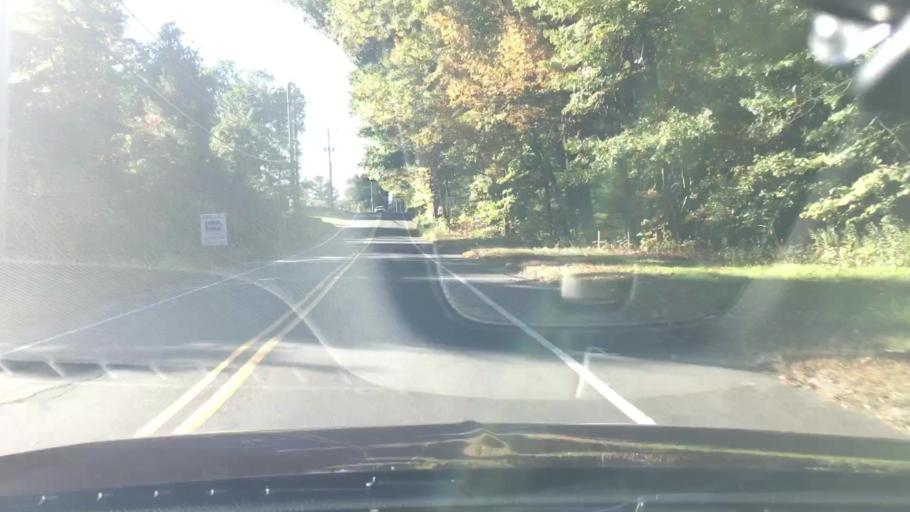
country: US
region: Connecticut
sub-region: Hartford County
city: Blue Hills
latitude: 41.8527
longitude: -72.7104
